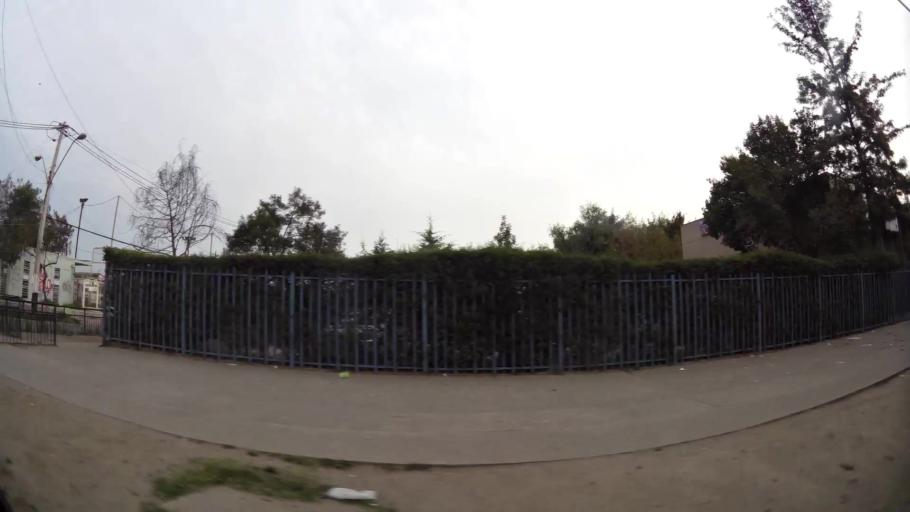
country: CL
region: Santiago Metropolitan
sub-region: Provincia de Santiago
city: Lo Prado
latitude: -33.5136
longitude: -70.7947
